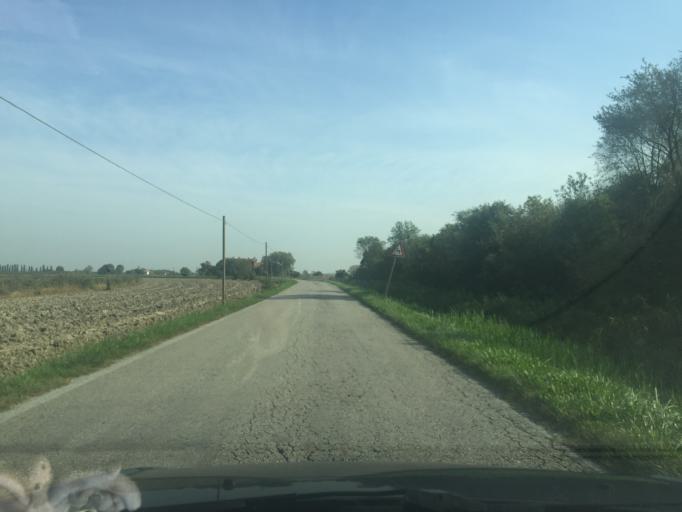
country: IT
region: Veneto
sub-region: Provincia di Venezia
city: Passarella
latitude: 45.6192
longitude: 12.6422
